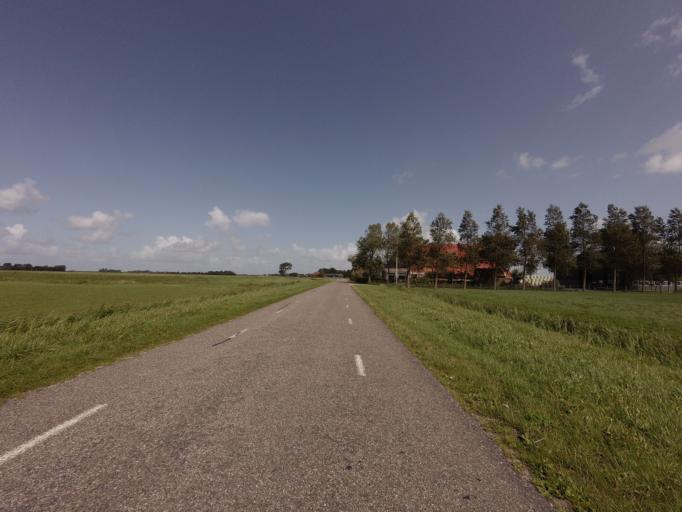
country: NL
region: Friesland
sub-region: Sudwest Fryslan
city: Makkum
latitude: 53.1044
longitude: 5.4311
